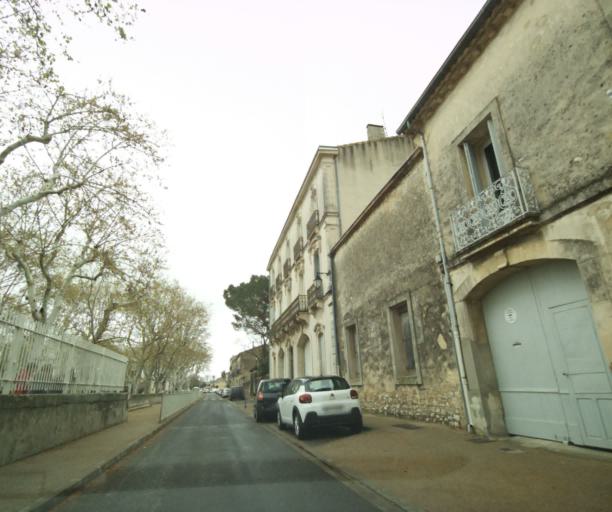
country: FR
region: Languedoc-Roussillon
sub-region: Departement de l'Herault
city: Cournonterral
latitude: 43.5562
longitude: 3.7196
